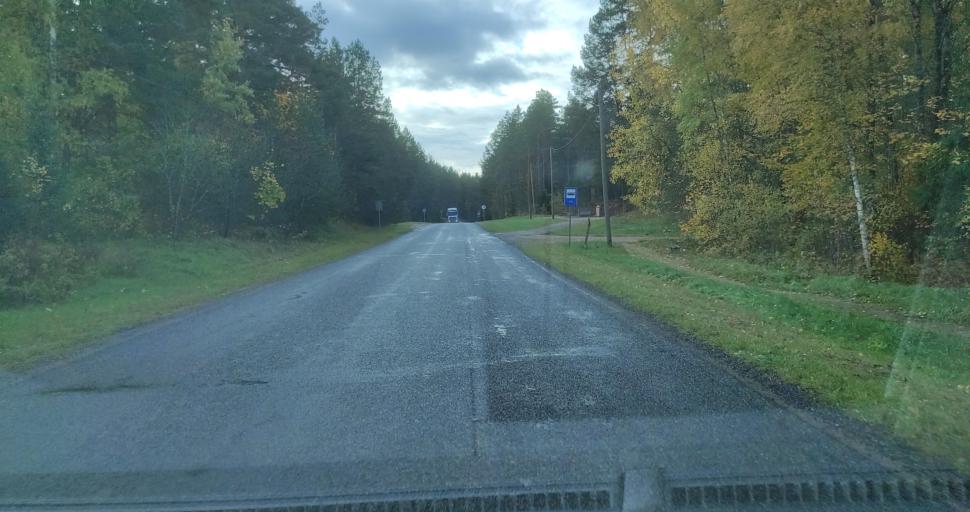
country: LV
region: Skrunda
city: Skrunda
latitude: 56.6638
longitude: 22.0232
